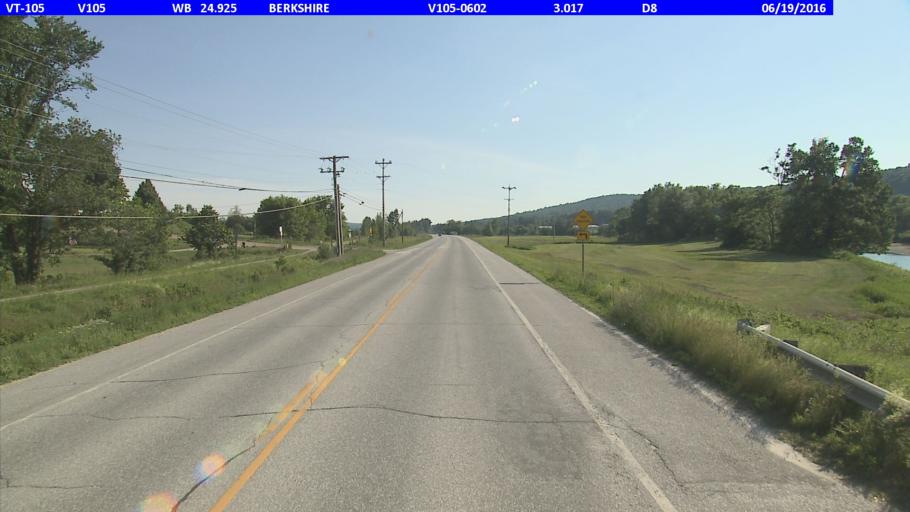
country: US
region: Vermont
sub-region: Franklin County
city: Richford
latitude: 44.9622
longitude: -72.6930
